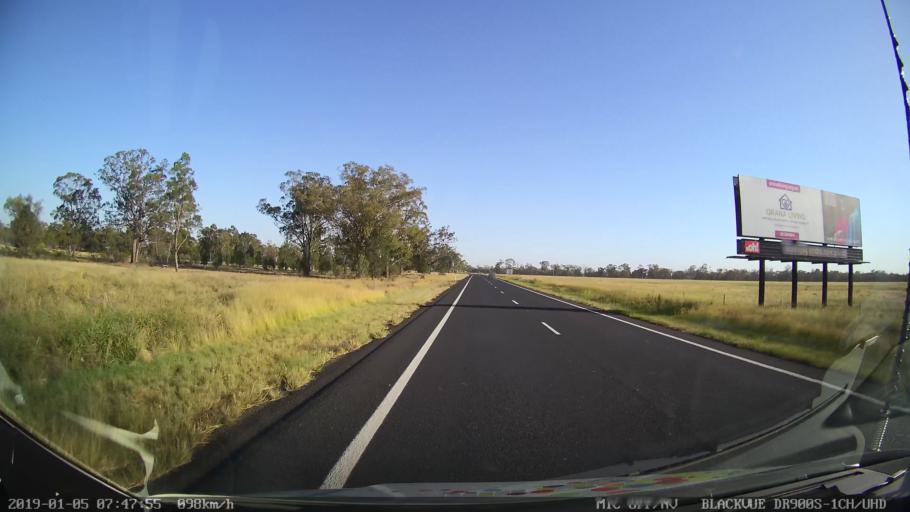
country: AU
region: New South Wales
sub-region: Gilgandra
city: Gilgandra
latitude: -31.8240
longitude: 148.6387
